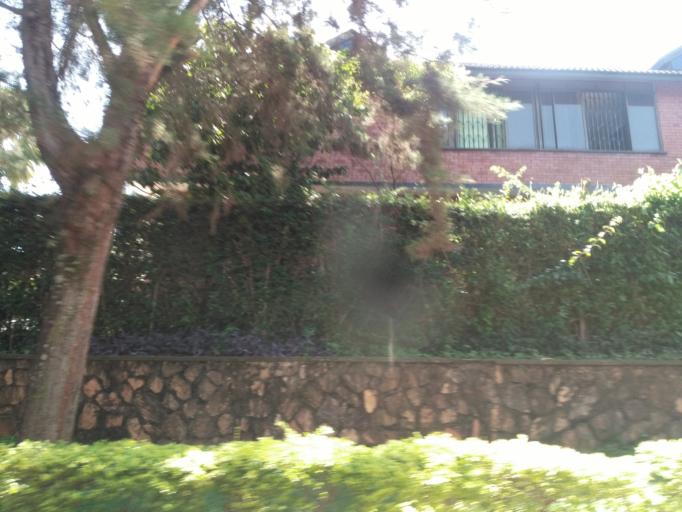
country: UG
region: Central Region
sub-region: Kampala District
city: Kampala
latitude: 0.3230
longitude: 32.5860
